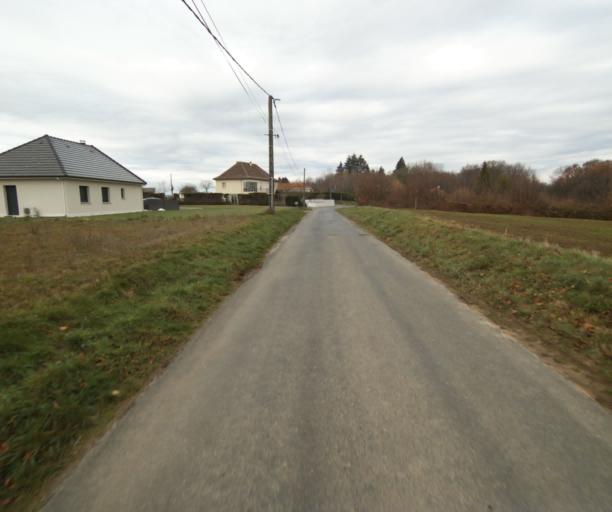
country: FR
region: Limousin
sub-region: Departement de la Correze
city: Laguenne
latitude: 45.2299
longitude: 1.7623
